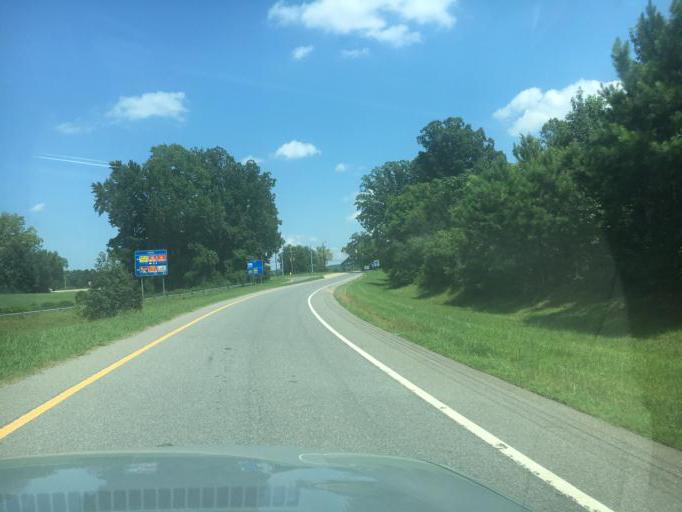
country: US
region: North Carolina
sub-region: Cleveland County
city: Kings Mountain
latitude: 35.2232
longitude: -81.3359
